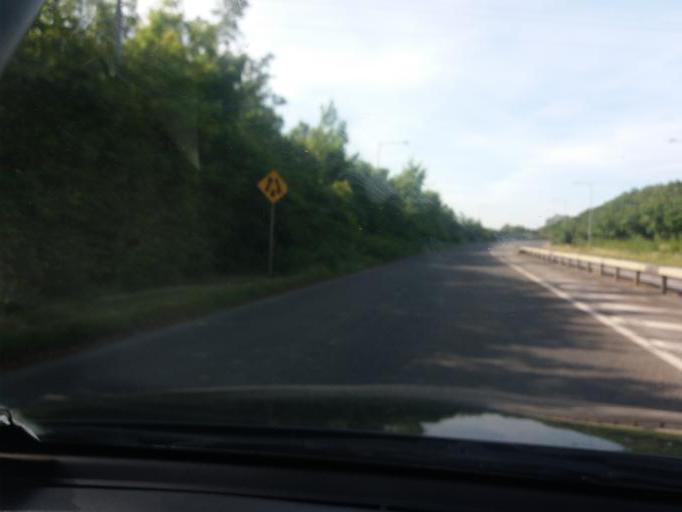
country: IE
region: Leinster
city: Balrothery
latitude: 53.5531
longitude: -6.2107
